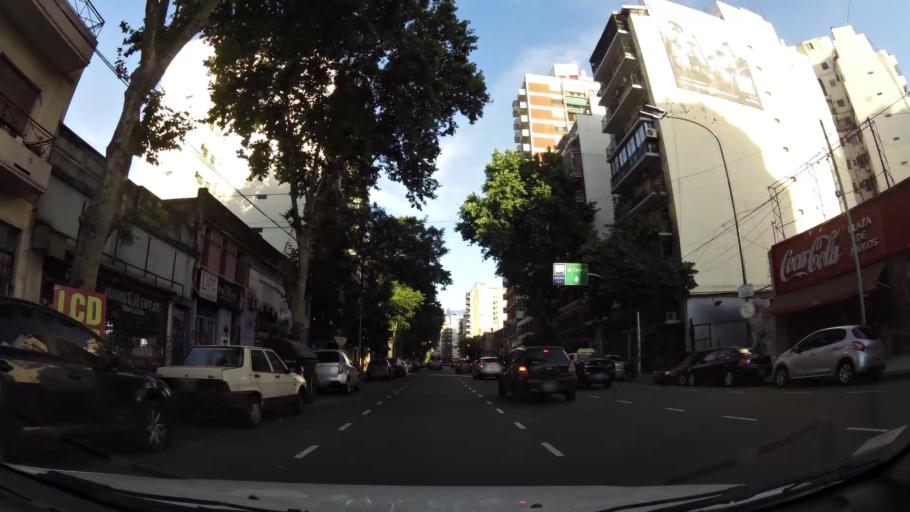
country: AR
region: Buenos Aires F.D.
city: Colegiales
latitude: -34.6079
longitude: -58.4448
